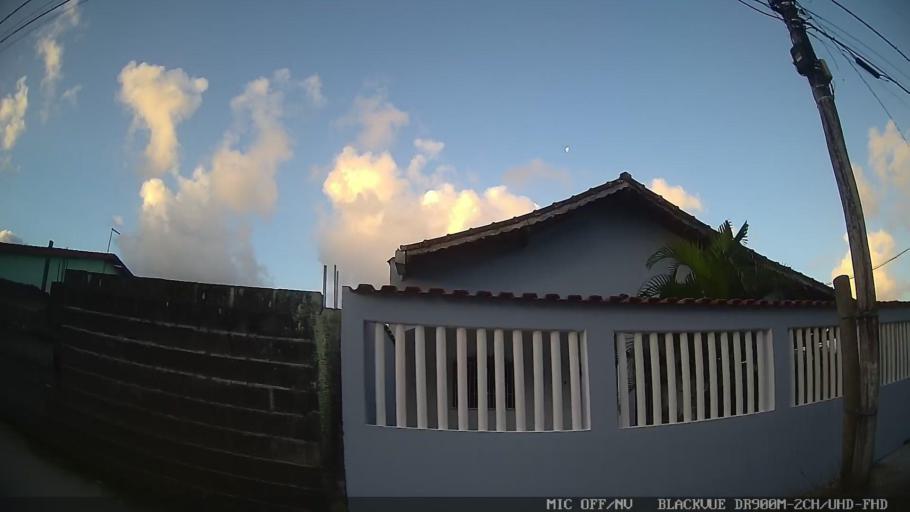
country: BR
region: Sao Paulo
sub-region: Itanhaem
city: Itanhaem
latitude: -24.1444
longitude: -46.7306
